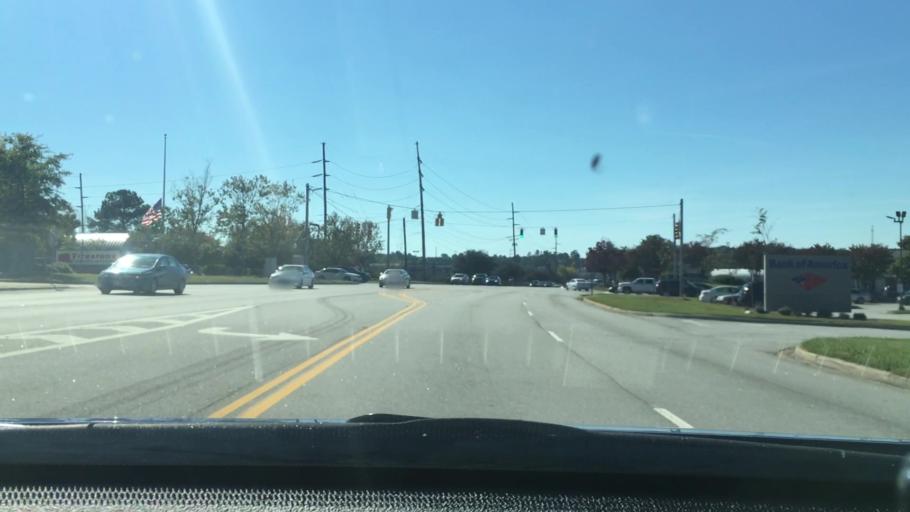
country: US
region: South Carolina
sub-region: Lexington County
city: Seven Oaks
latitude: 34.0743
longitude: -81.1559
